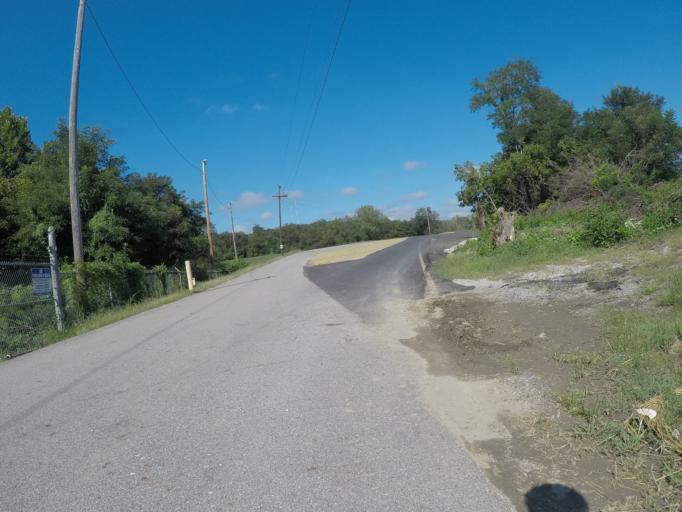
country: US
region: Kentucky
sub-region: Boyd County
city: Catlettsburg
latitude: 38.4084
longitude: -82.5912
